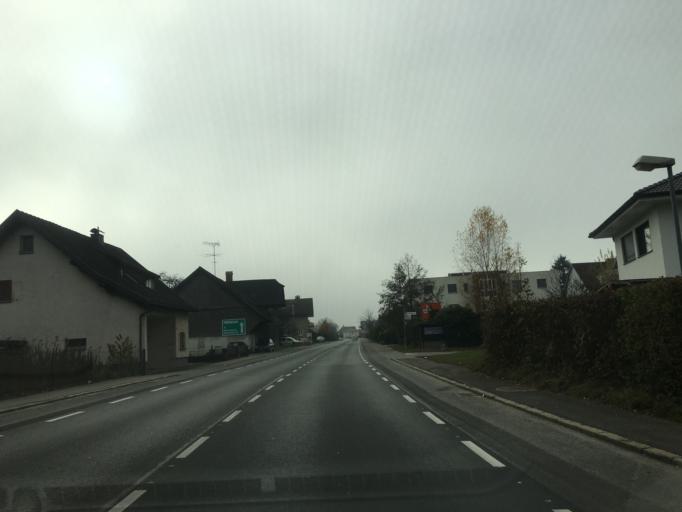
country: AT
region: Vorarlberg
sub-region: Politischer Bezirk Feldkirch
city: Gotzis
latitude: 47.3196
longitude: 9.6233
